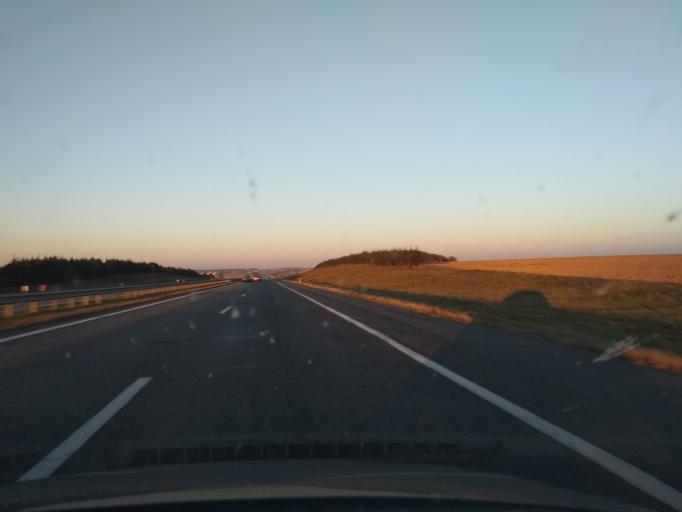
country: BY
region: Minsk
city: Snow
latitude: 53.3299
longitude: 26.4215
